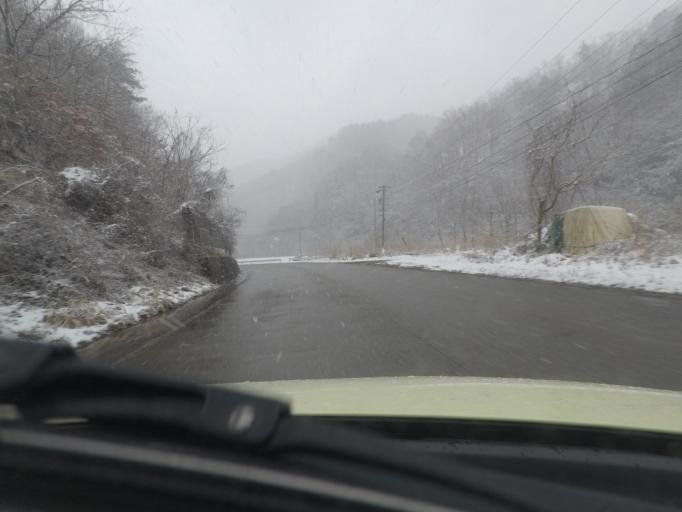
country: JP
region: Gifu
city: Takayama
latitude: 36.1359
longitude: 137.3286
